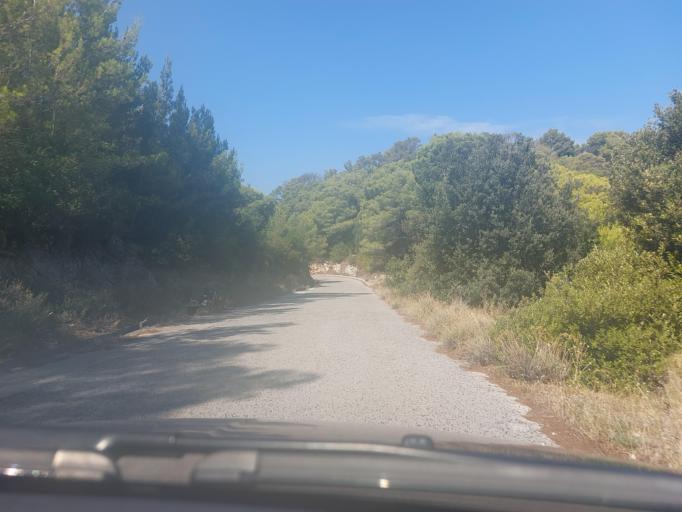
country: HR
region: Dubrovacko-Neretvanska
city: Smokvica
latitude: 42.7489
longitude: 16.8450
